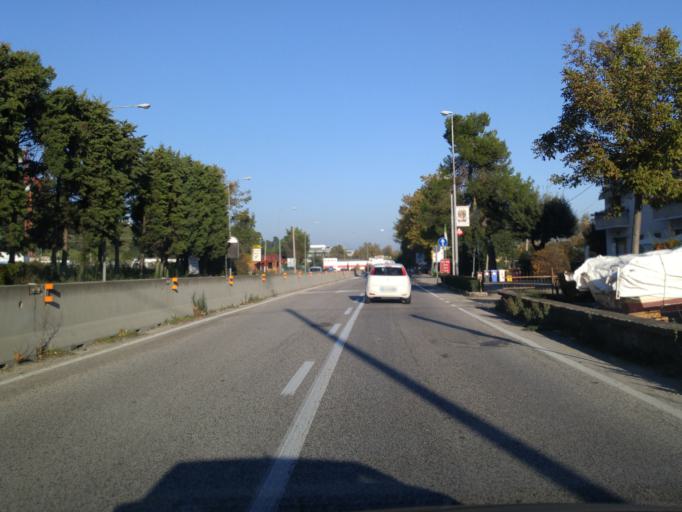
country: IT
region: The Marches
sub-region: Provincia di Pesaro e Urbino
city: Pesaro
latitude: 43.9046
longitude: 12.8569
